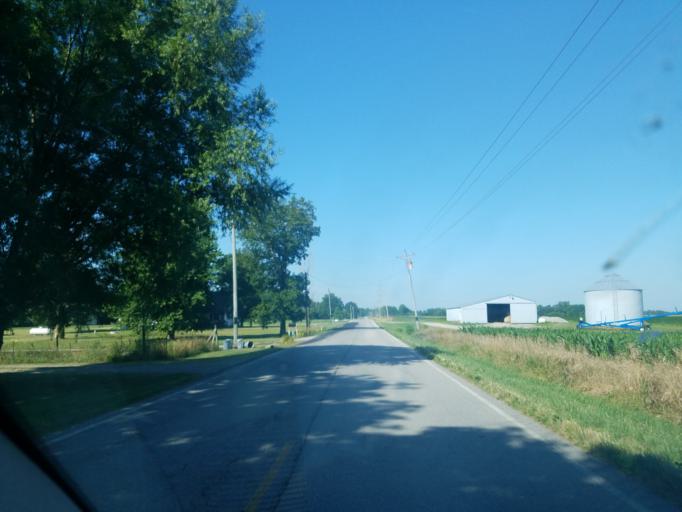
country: US
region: Ohio
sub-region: Union County
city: Richwood
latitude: 40.4200
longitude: -83.4396
